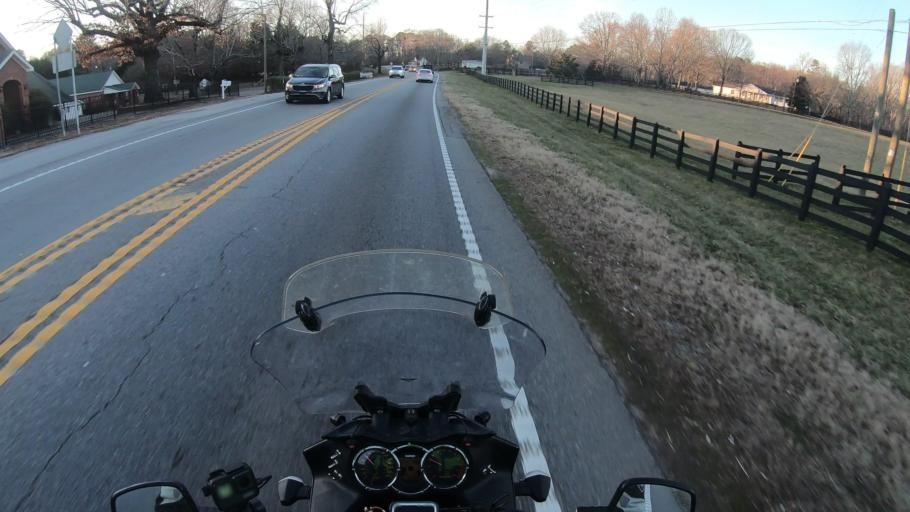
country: US
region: Georgia
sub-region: Forsyth County
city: Cumming
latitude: 34.2982
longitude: -84.1632
